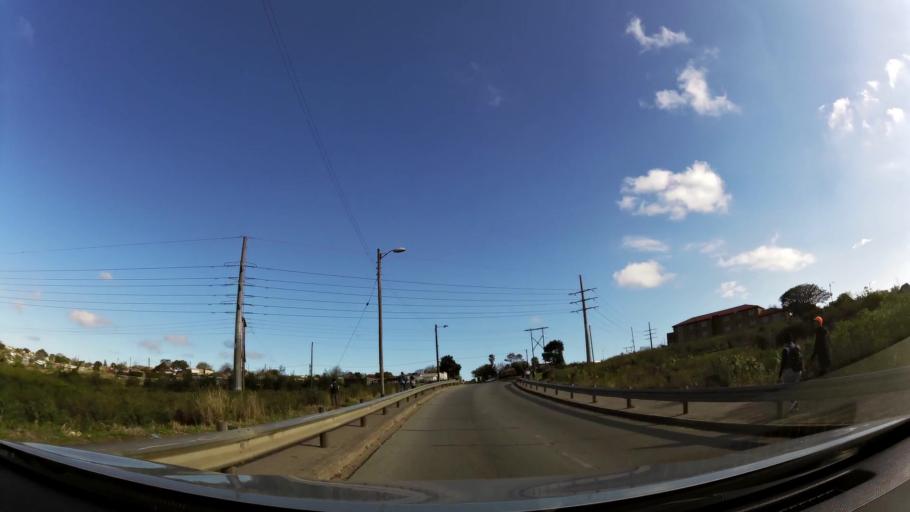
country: ZA
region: Western Cape
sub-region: Eden District Municipality
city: George
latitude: -33.9798
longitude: 22.4765
